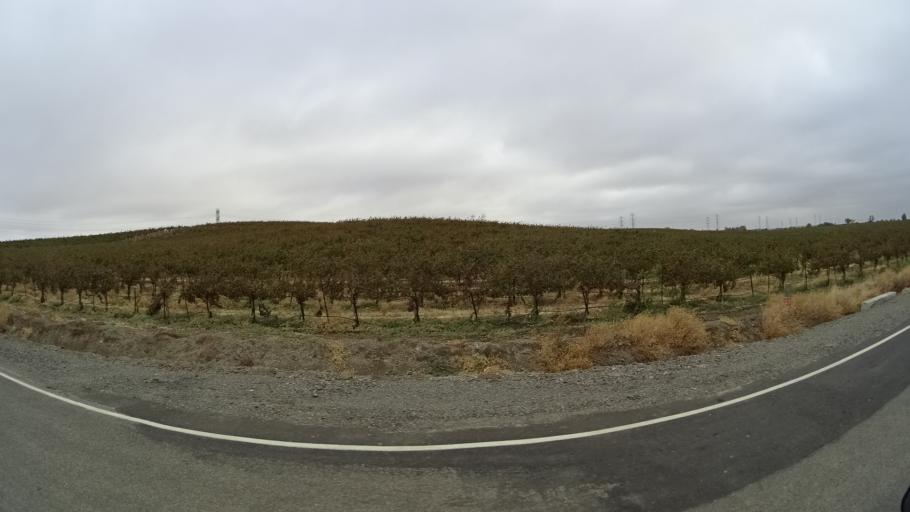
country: US
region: California
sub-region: Yolo County
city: Dunnigan
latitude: 38.8207
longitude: -122.0433
